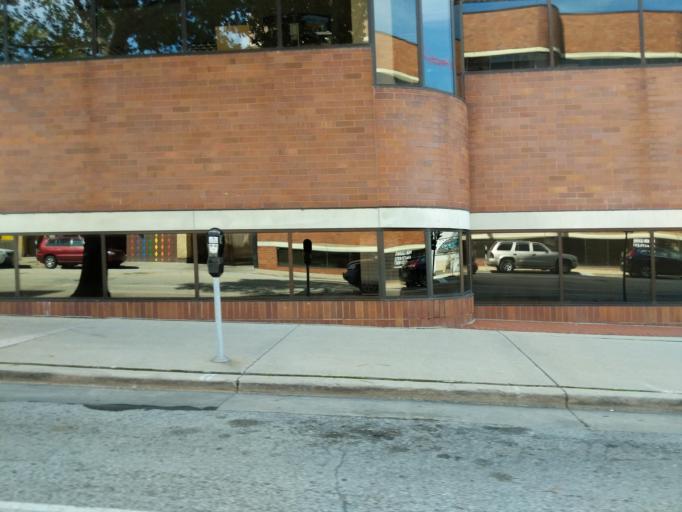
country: US
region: Wisconsin
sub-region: Milwaukee County
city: Milwaukee
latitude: 43.0412
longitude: -87.9063
